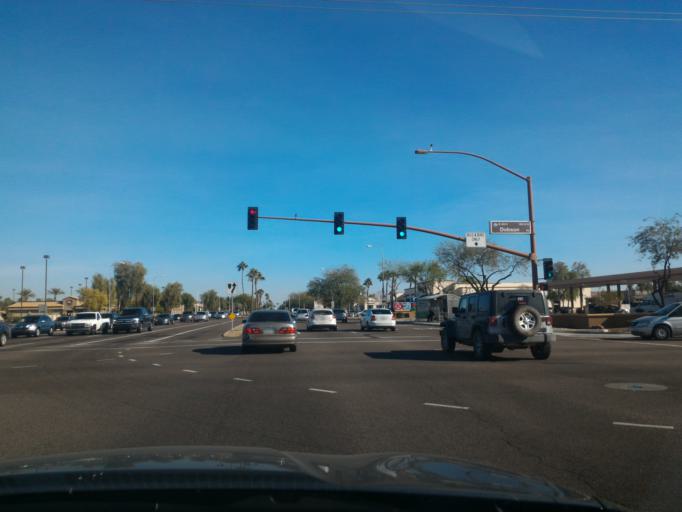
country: US
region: Arizona
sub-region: Maricopa County
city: Chandler
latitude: 33.3059
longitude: -111.8764
